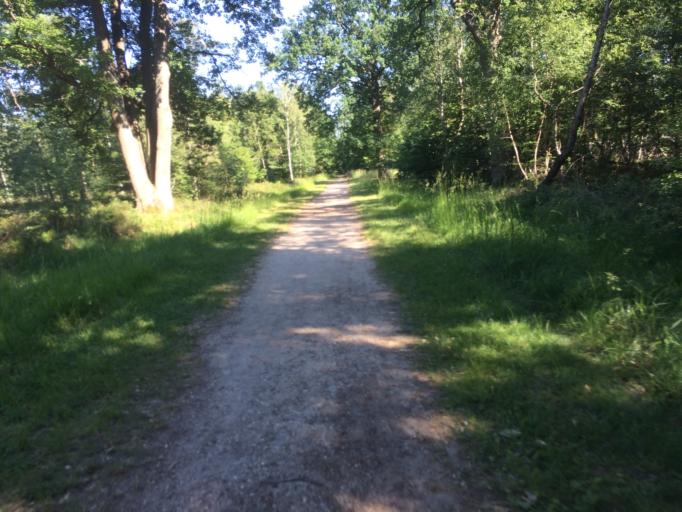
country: FR
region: Ile-de-France
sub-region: Departement du Val-de-Marne
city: Boissy-Saint-Leger
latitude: 48.7495
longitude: 2.5293
